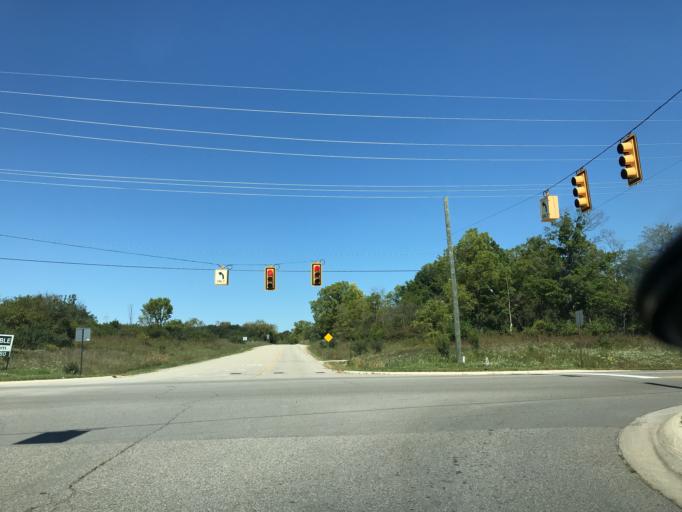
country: US
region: Michigan
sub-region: Washtenaw County
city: Ypsilanti
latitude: 42.2748
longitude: -83.6230
